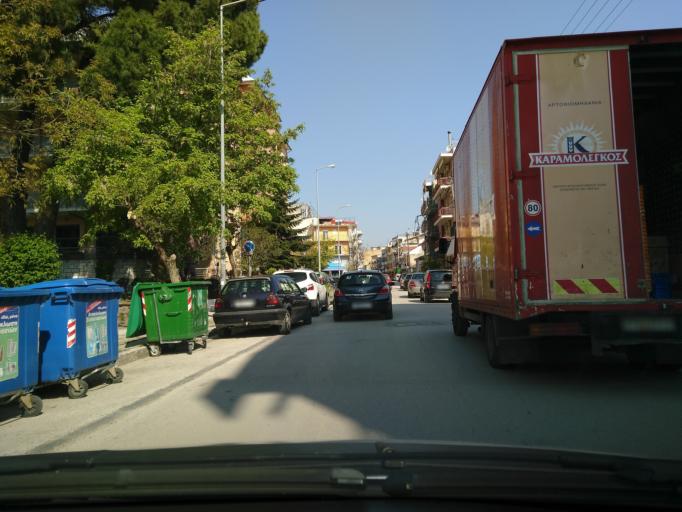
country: GR
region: Epirus
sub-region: Nomos Ioanninon
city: Ioannina
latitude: 39.6740
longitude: 20.8445
